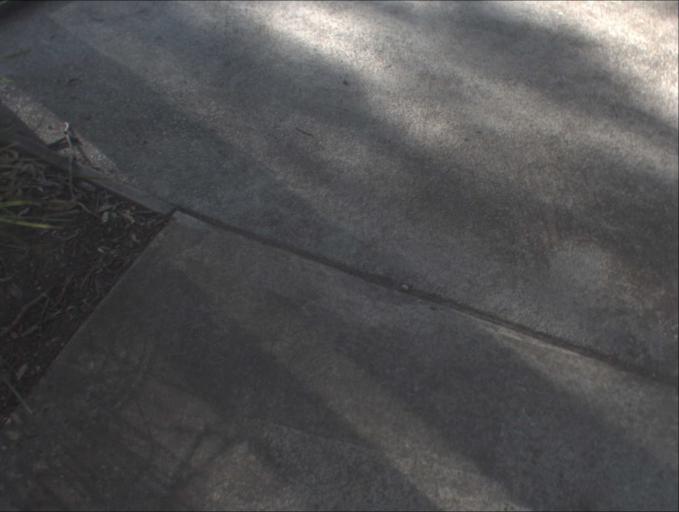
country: AU
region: Queensland
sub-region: Logan
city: Waterford West
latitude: -27.7108
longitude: 153.1558
